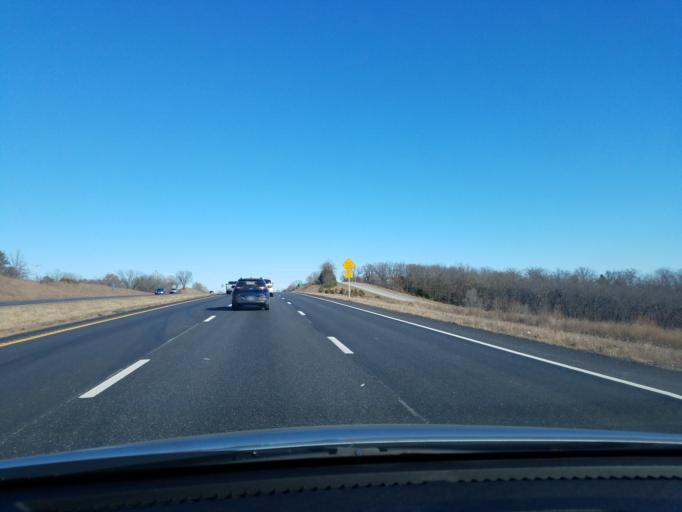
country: US
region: Missouri
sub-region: Taney County
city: Hollister
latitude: 36.5712
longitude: -93.2483
